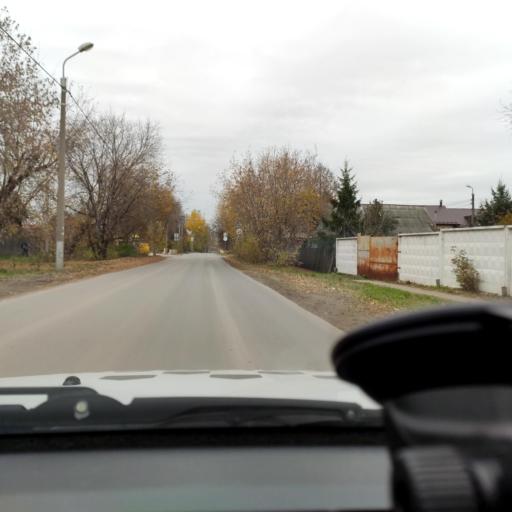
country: RU
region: Perm
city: Perm
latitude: 57.9934
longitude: 56.3084
